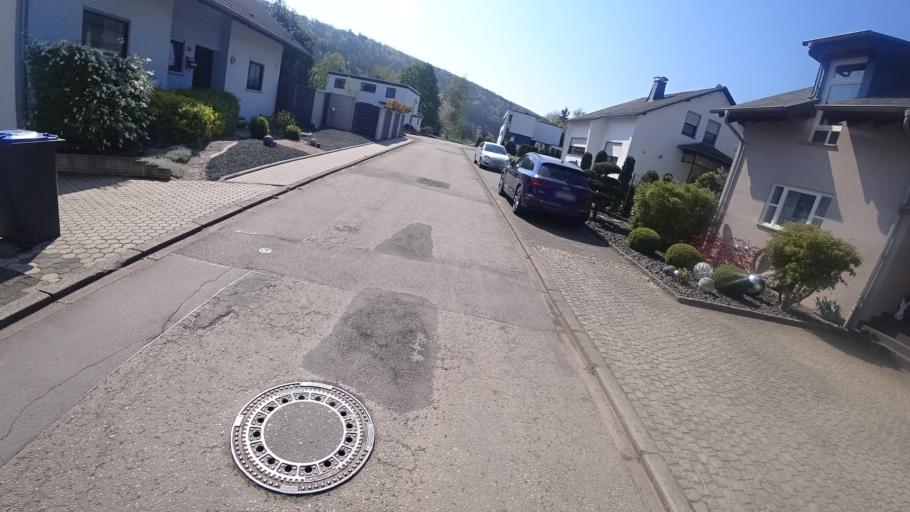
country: DE
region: Rheinland-Pfalz
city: Tawern
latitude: 49.6690
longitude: 6.5144
